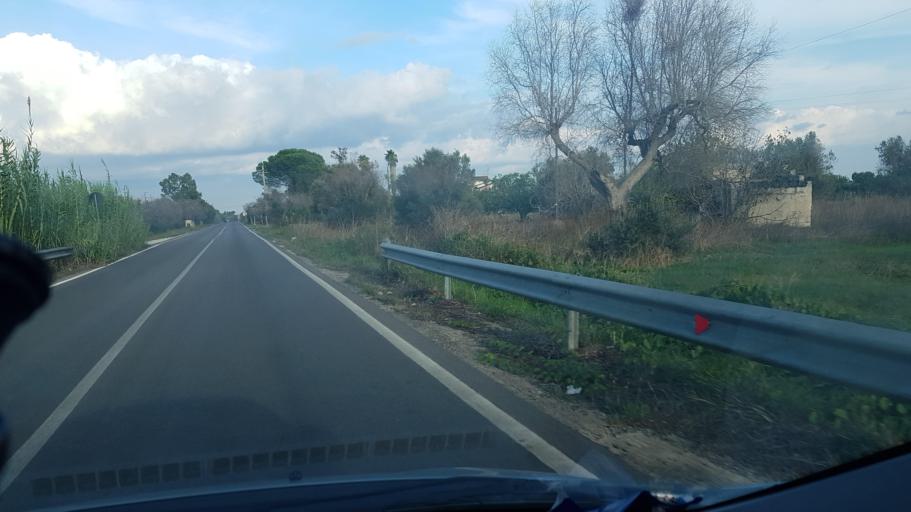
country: IT
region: Apulia
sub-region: Provincia di Lecce
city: Veglie
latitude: 40.3367
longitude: 17.9883
